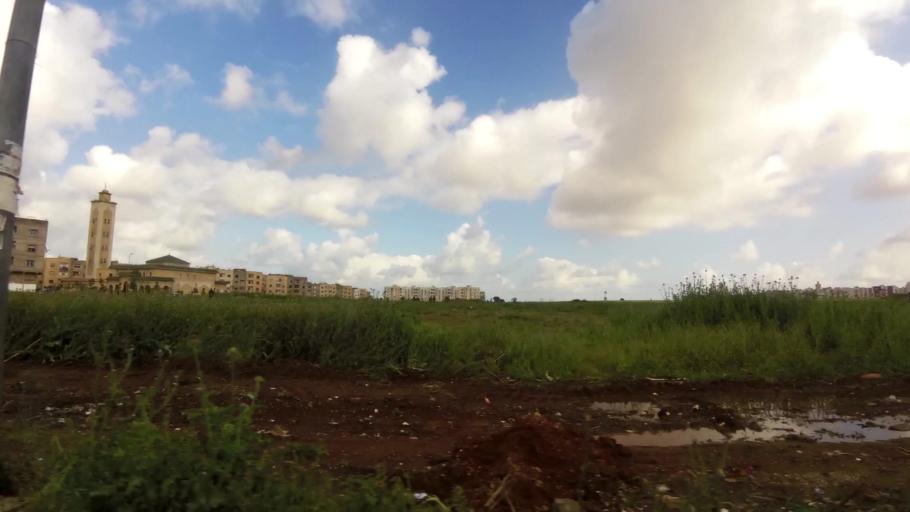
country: MA
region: Grand Casablanca
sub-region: Nouaceur
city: Bouskoura
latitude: 33.5323
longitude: -7.7003
